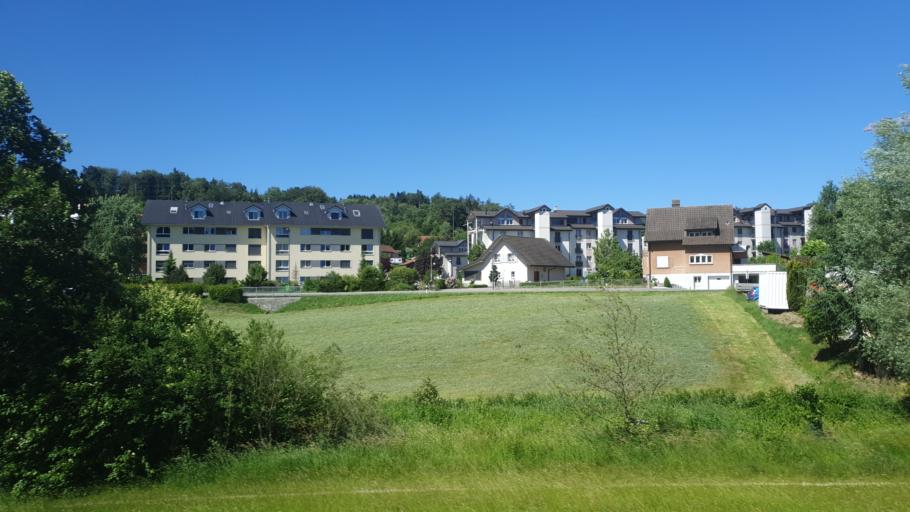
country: CH
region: Fribourg
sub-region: Sarine District
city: Belfaux
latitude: 46.8615
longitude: 7.1257
